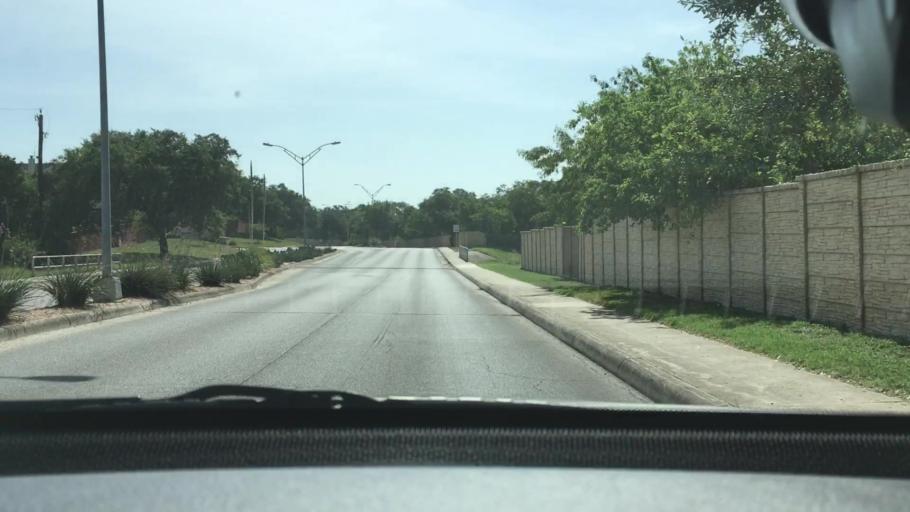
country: US
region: Texas
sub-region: Bexar County
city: Live Oak
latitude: 29.5879
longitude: -98.4023
